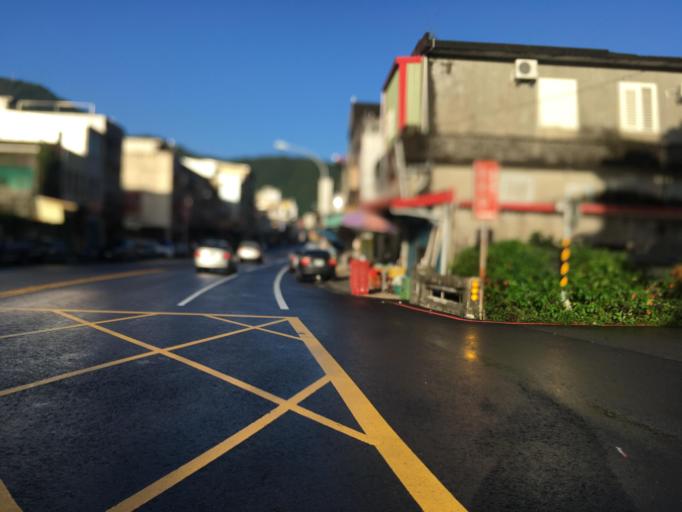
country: TW
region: Taiwan
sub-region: Yilan
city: Yilan
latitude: 24.5956
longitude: 121.8428
